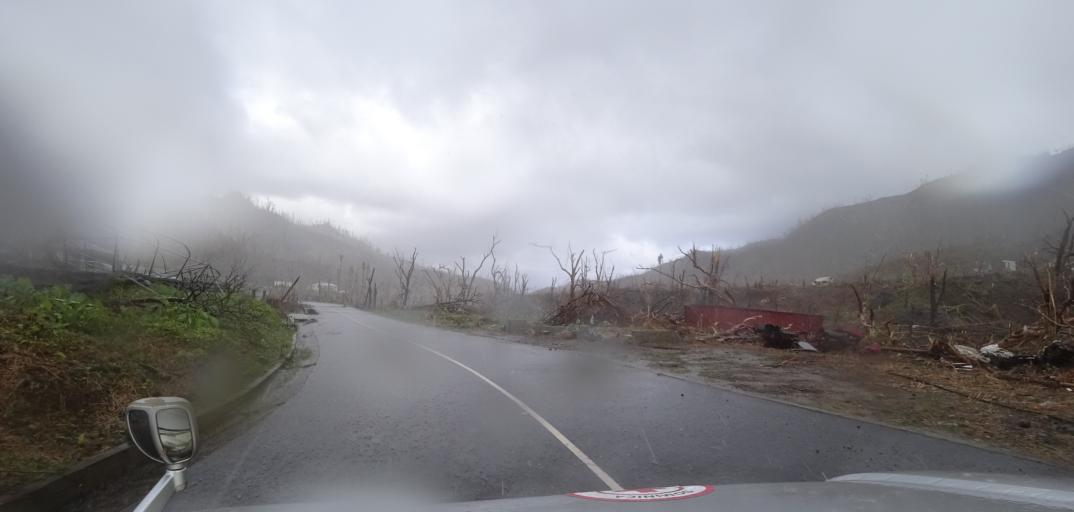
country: DM
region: Saint Andrew
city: Marigot
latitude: 15.4877
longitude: -61.2771
